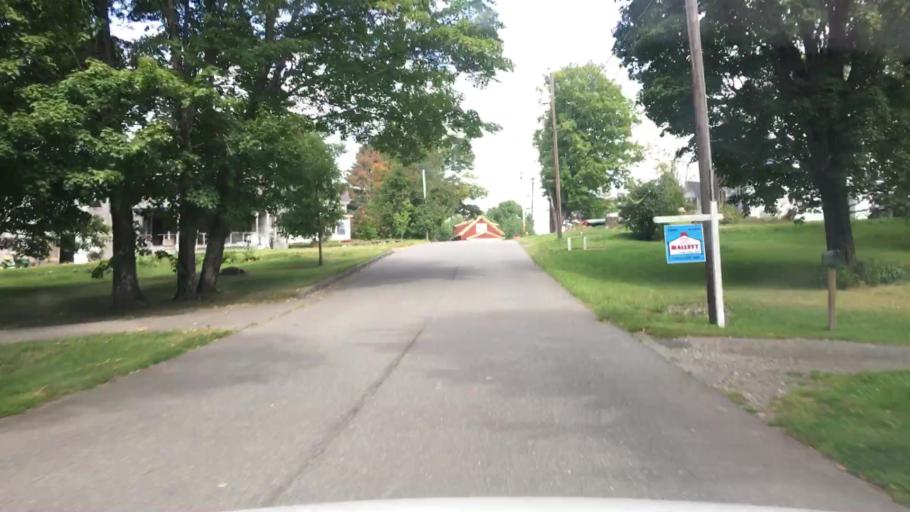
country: US
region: Maine
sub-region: Piscataquis County
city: Dover-Foxcroft
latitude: 45.1899
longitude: -69.2230
